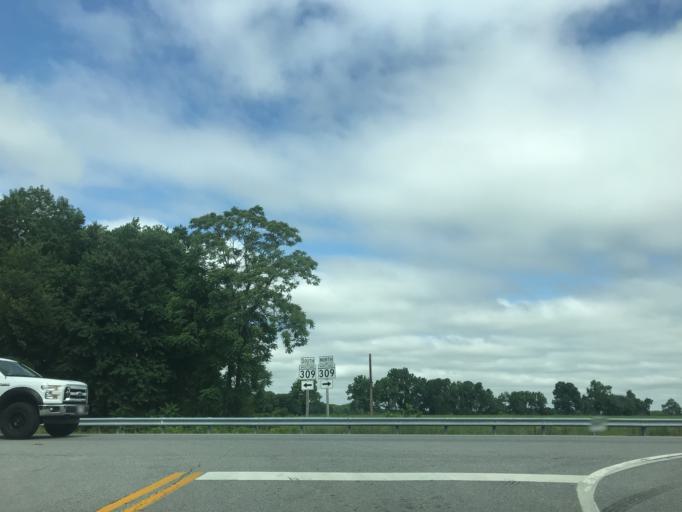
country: US
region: Maryland
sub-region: Caroline County
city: Ridgely
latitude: 38.8879
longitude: -75.9858
